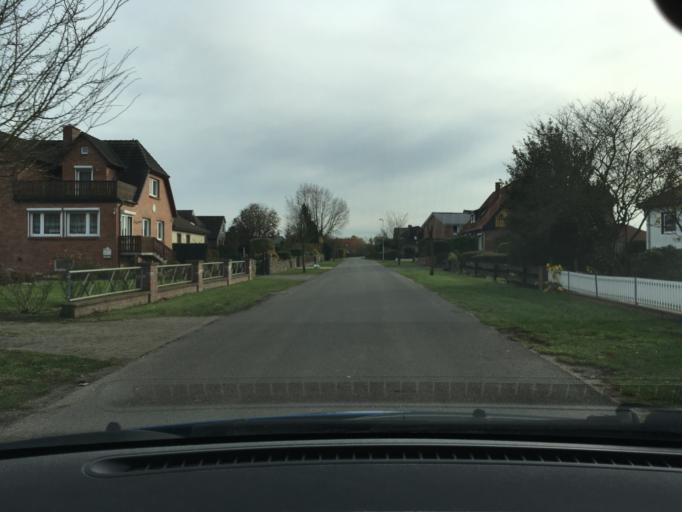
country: DE
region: Lower Saxony
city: Wittorf
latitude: 53.3275
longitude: 10.3649
